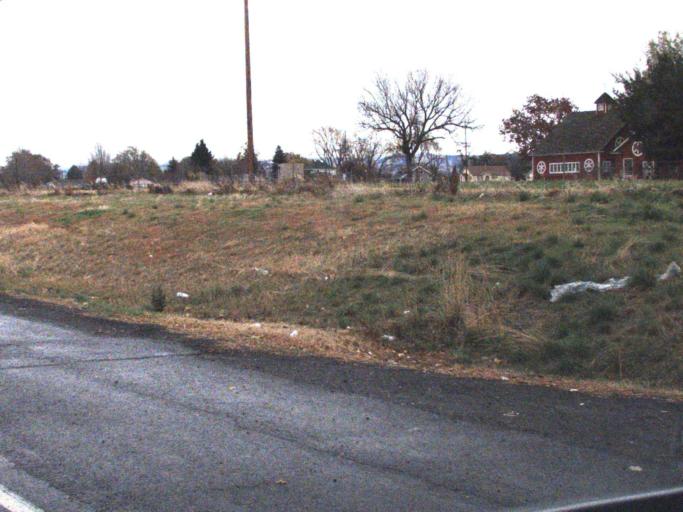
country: US
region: Washington
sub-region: Walla Walla County
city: Walla Walla
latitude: 46.0809
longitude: -118.3282
